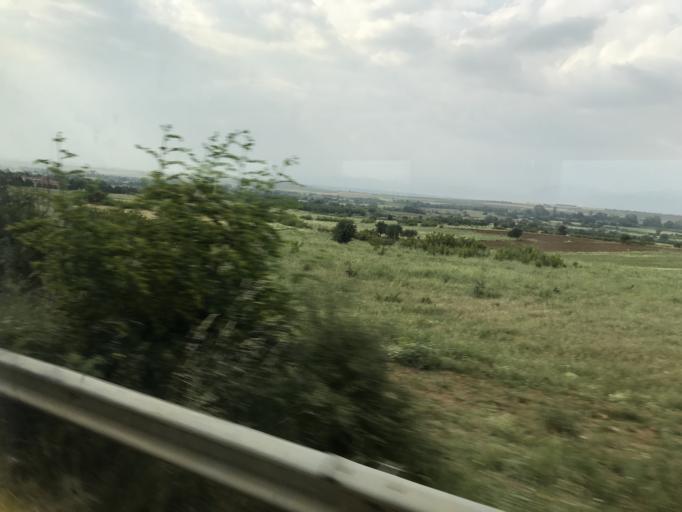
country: GR
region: East Macedonia and Thrace
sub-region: Nomos Rodopis
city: Sapes
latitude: 41.0304
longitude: 25.6840
